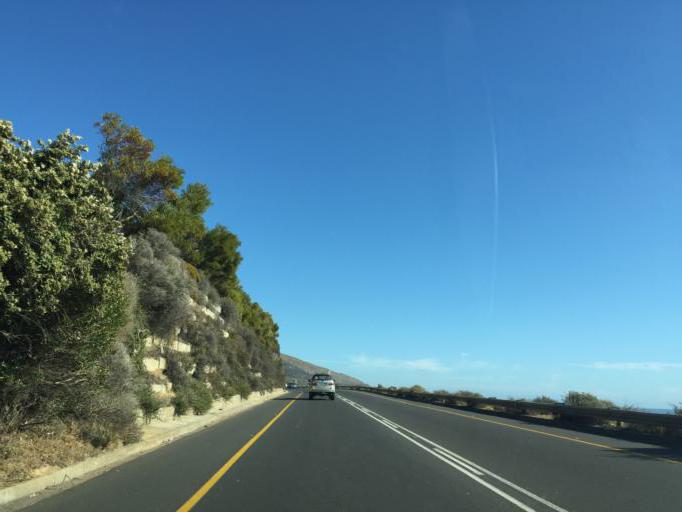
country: ZA
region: Western Cape
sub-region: City of Cape Town
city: Cape Town
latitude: -33.9753
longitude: 18.3693
